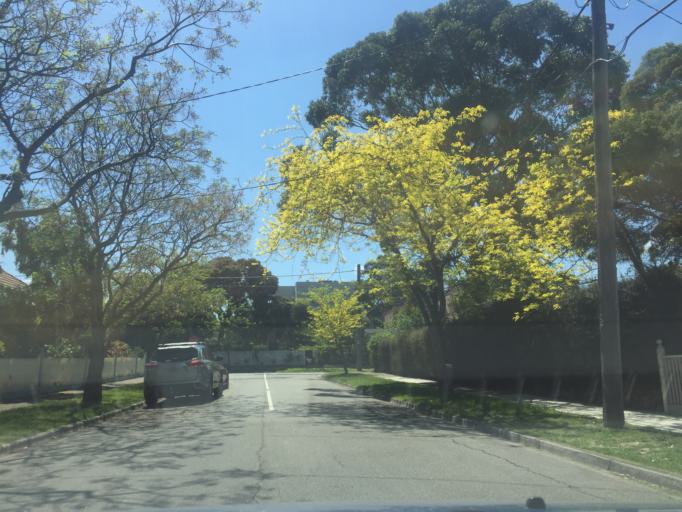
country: AU
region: Victoria
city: Ivanhoe East
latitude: -37.7688
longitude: 145.0519
